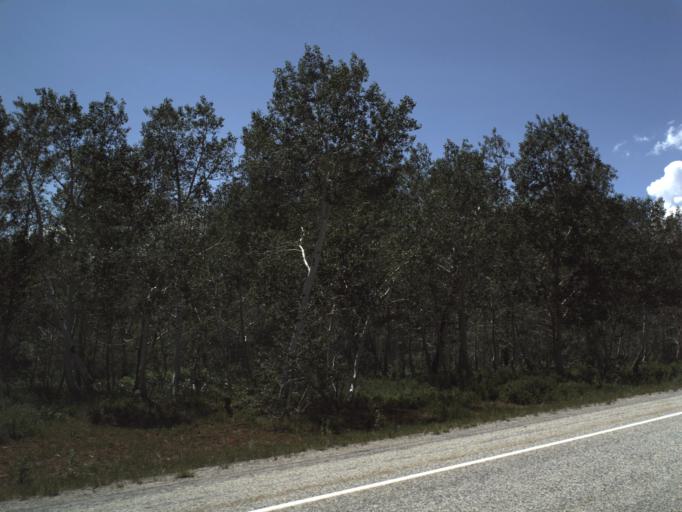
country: US
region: Utah
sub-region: Rich County
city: Randolph
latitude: 41.4720
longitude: -111.4776
